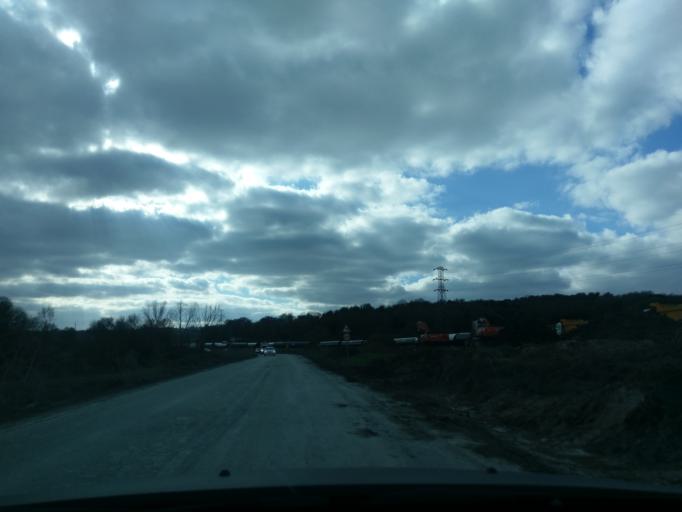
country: TR
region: Istanbul
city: Durusu
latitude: 41.2916
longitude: 28.6653
